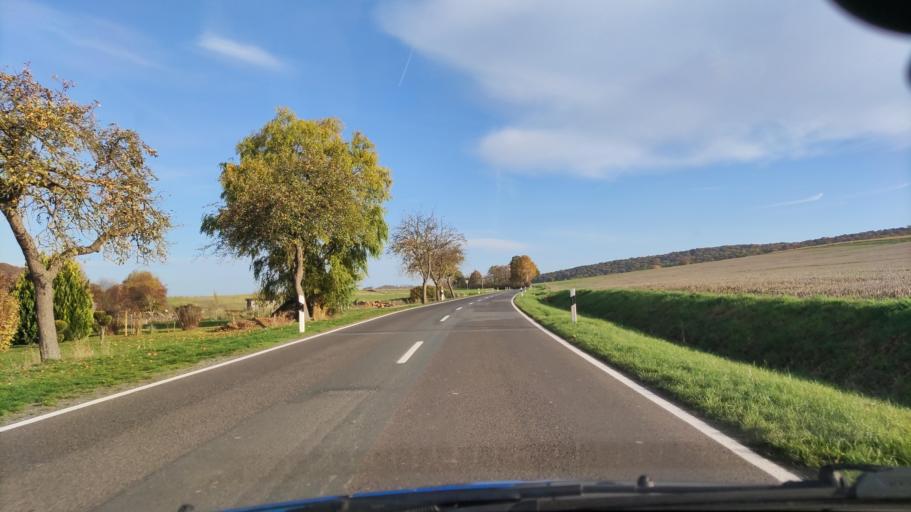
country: DE
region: Lower Saxony
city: Dassel
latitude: 51.7719
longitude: 9.7262
